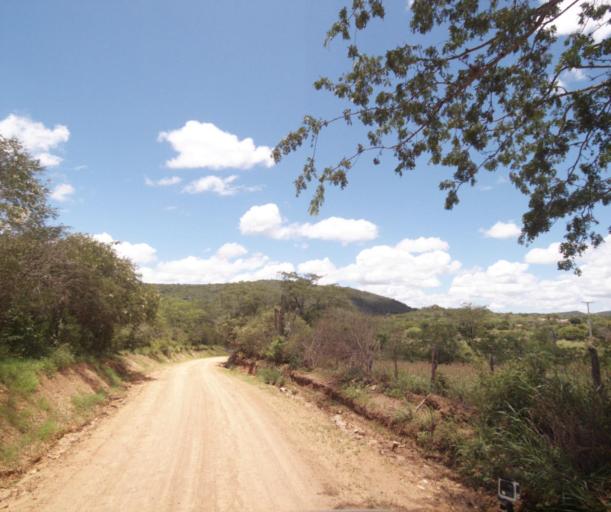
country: BR
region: Bahia
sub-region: Pocoes
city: Pocoes
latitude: -14.3820
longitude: -40.3788
